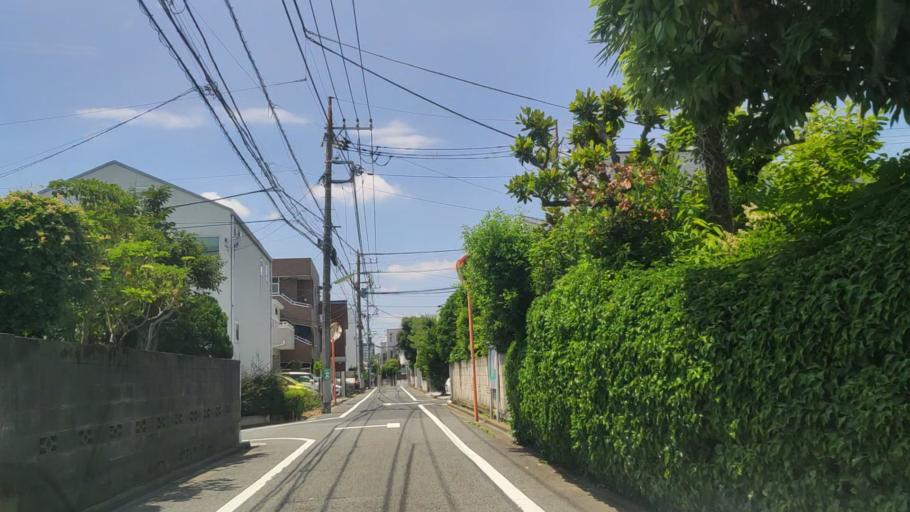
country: JP
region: Tokyo
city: Tokyo
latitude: 35.6630
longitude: 139.6451
